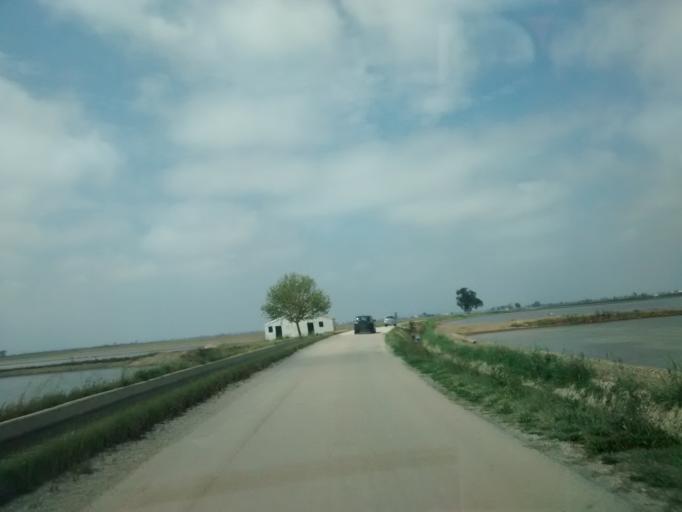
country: ES
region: Catalonia
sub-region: Provincia de Tarragona
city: Deltebre
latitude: 40.6841
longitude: 0.7896
